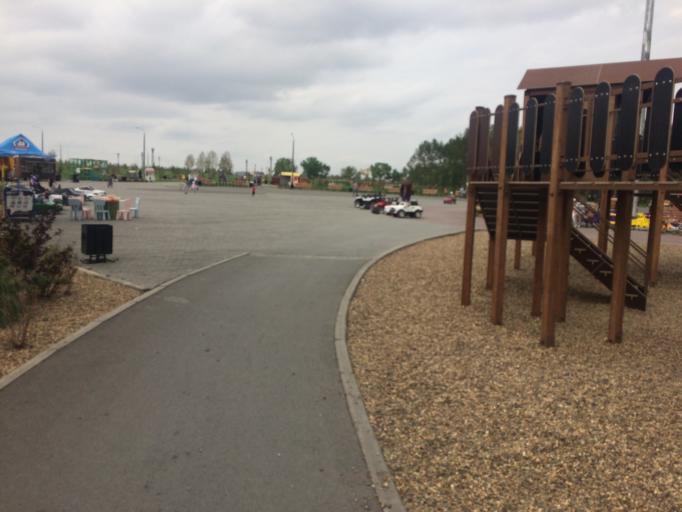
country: RU
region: Chelyabinsk
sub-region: Gorod Magnitogorsk
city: Magnitogorsk
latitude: 53.4041
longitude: 58.9888
